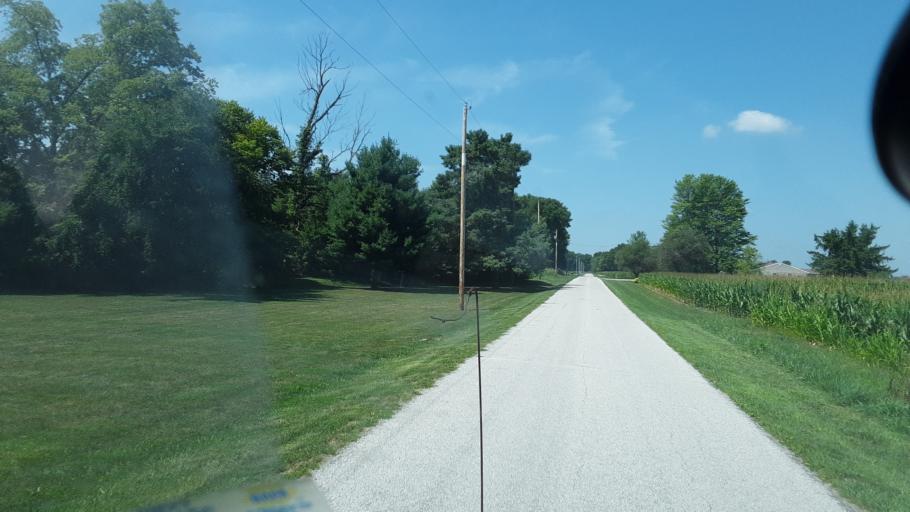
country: US
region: Ohio
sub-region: Hancock County
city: Findlay
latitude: 40.9922
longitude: -83.5254
